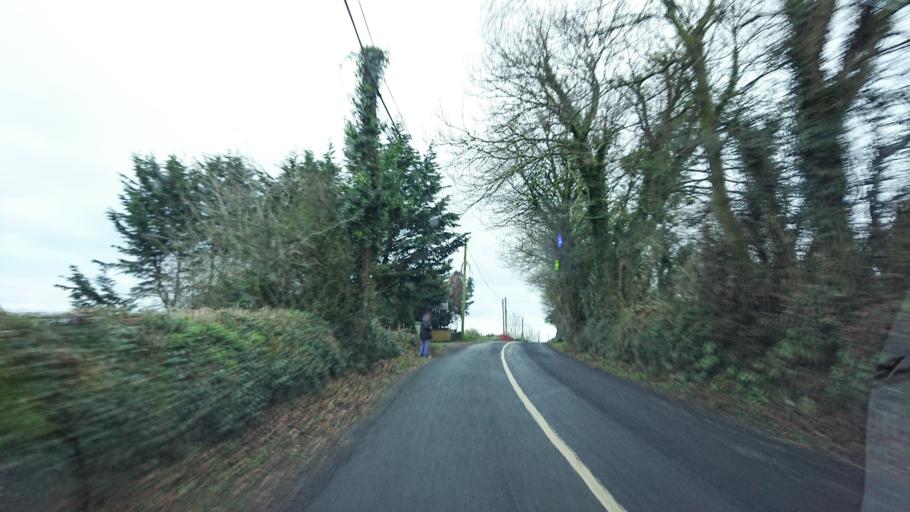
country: IE
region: Munster
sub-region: Waterford
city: Portlaw
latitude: 52.1678
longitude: -7.3914
